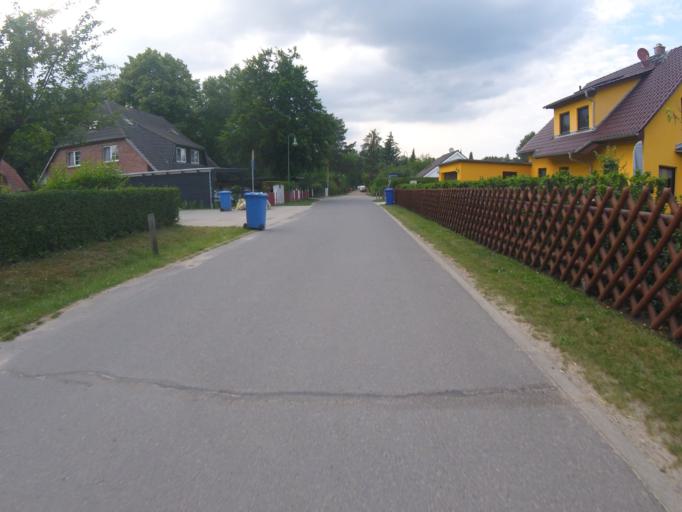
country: DE
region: Brandenburg
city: Bestensee
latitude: 52.2613
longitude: 13.6152
